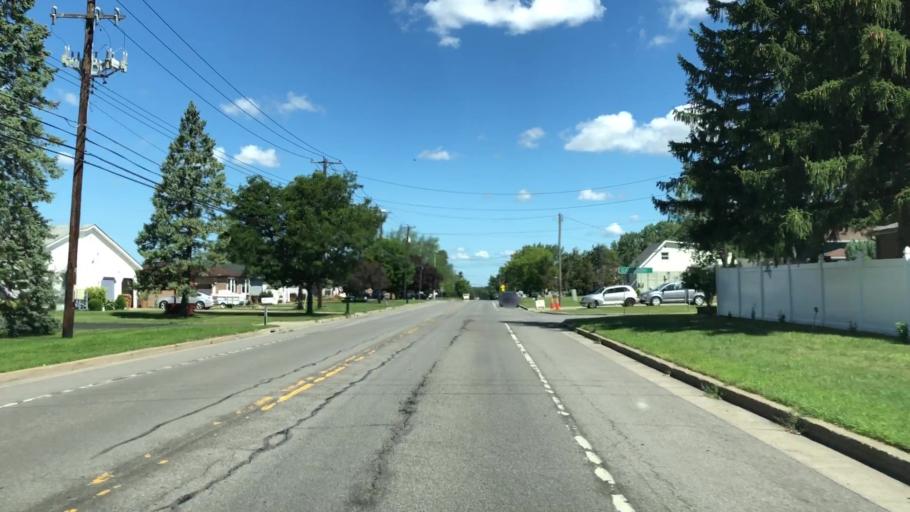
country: US
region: New York
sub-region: Erie County
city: Depew
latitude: 42.8750
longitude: -78.7089
